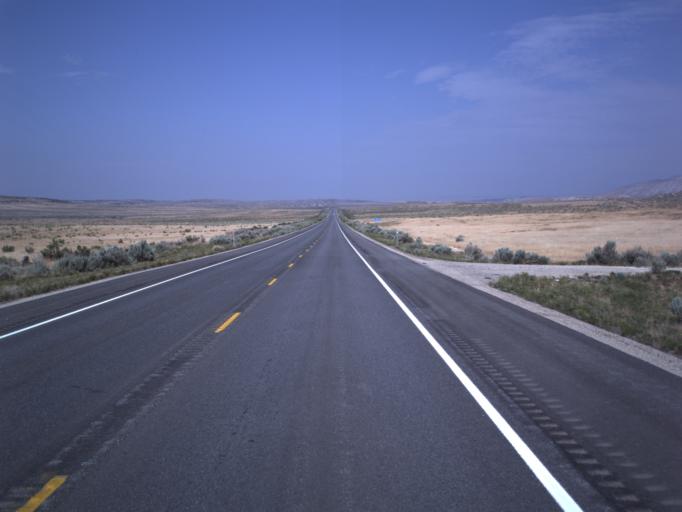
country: US
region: Colorado
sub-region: Rio Blanco County
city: Rangely
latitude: 40.2805
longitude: -109.0723
